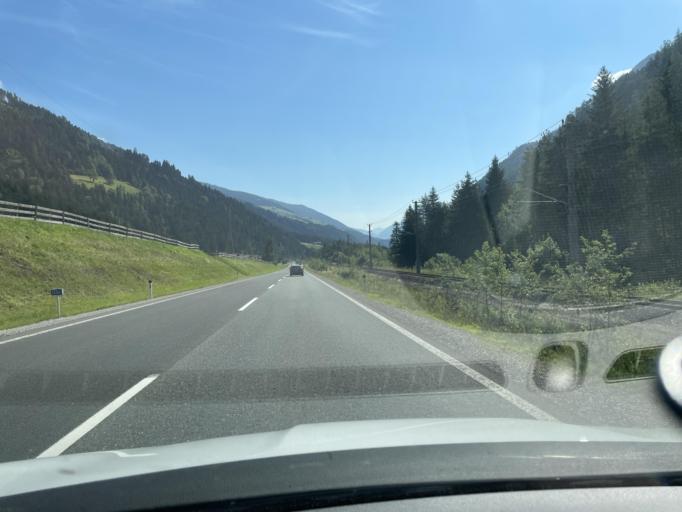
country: AT
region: Tyrol
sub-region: Politischer Bezirk Lienz
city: Anras
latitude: 46.7705
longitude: 12.6037
